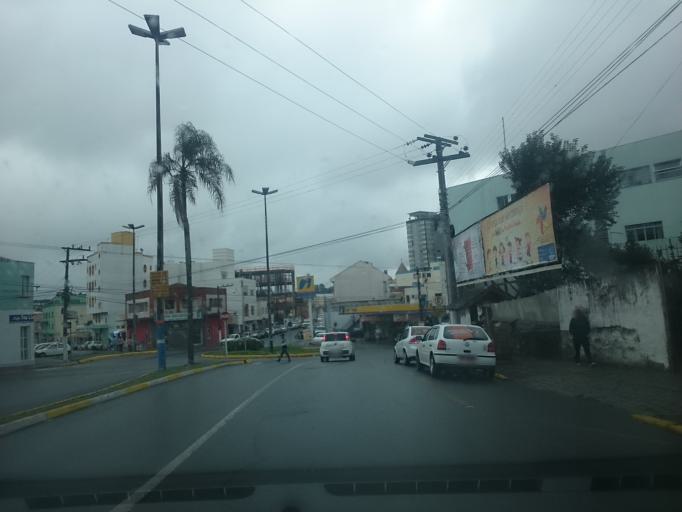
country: BR
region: Santa Catarina
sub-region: Lages
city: Lages
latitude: -27.8172
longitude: -50.3316
